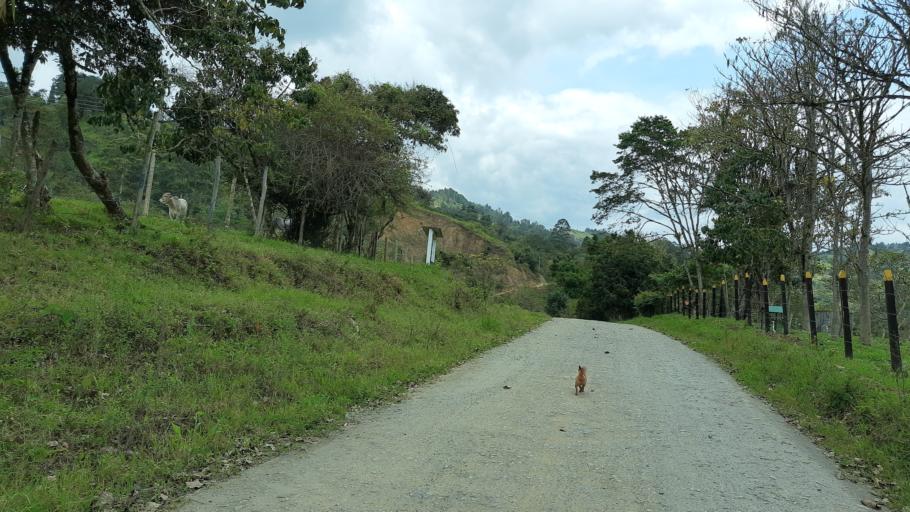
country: CO
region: Boyaca
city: Garagoa
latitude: 5.0665
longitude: -73.3623
